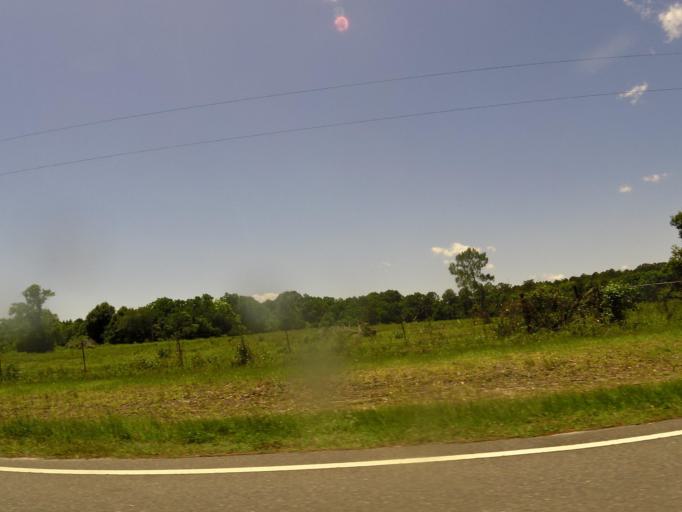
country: US
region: Florida
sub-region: Union County
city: Lake Butler
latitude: 30.0516
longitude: -82.2325
